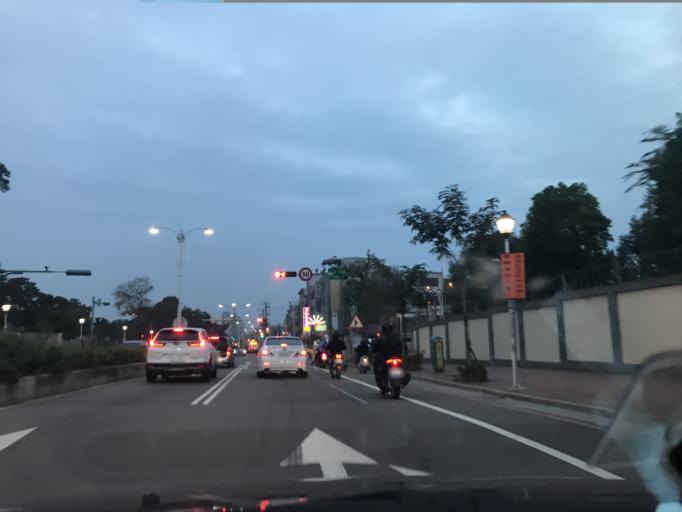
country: TW
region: Taiwan
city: Daxi
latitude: 24.9324
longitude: 121.2376
